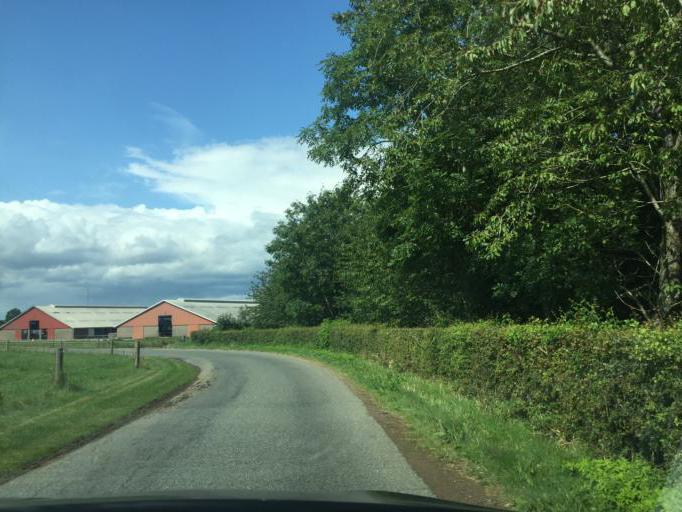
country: DK
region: South Denmark
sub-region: Faaborg-Midtfyn Kommune
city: Arslev
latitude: 55.3260
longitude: 10.4859
